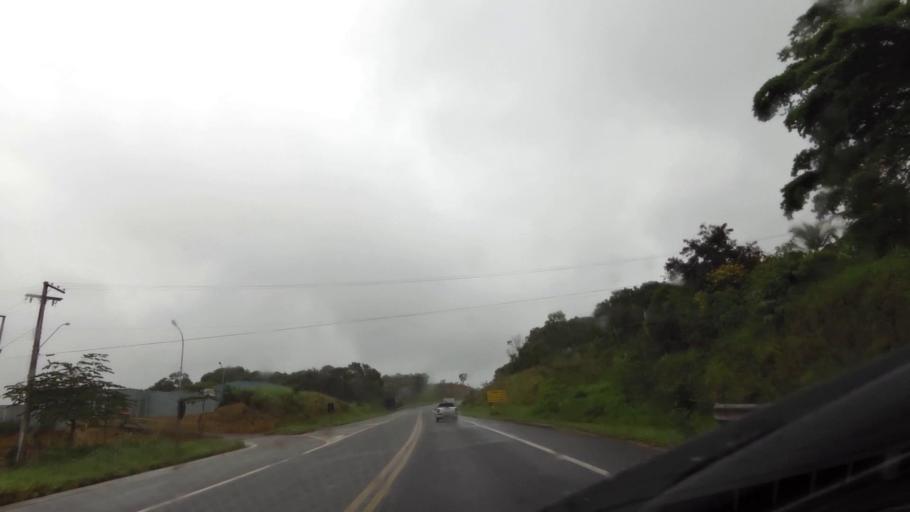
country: BR
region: Espirito Santo
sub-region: Guarapari
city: Guarapari
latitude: -20.7342
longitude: -40.5549
